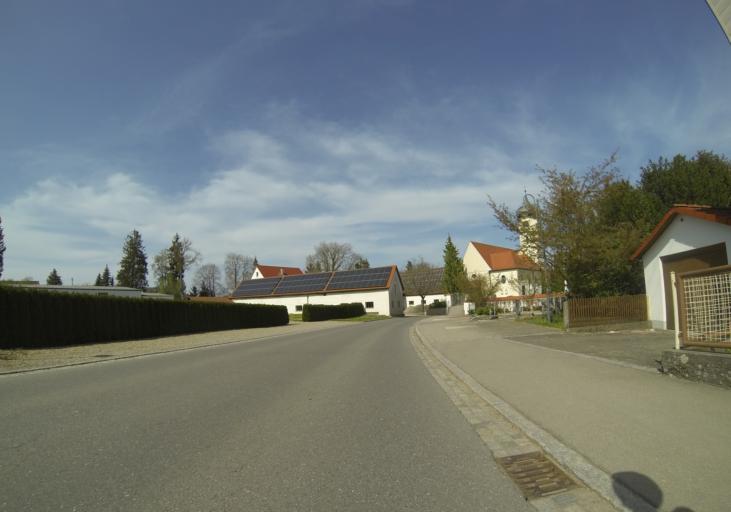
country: DE
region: Baden-Wuerttemberg
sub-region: Tuebingen Region
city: Achstetten
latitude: 48.2465
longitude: 9.9063
